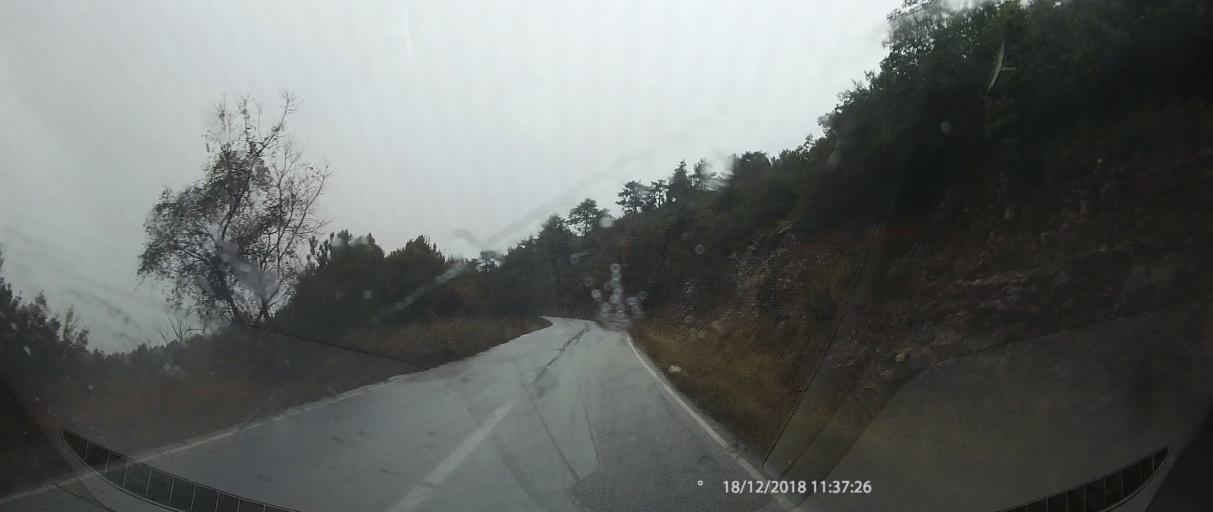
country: GR
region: Central Macedonia
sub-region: Nomos Pierias
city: Litochoro
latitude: 40.1171
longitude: 22.4786
